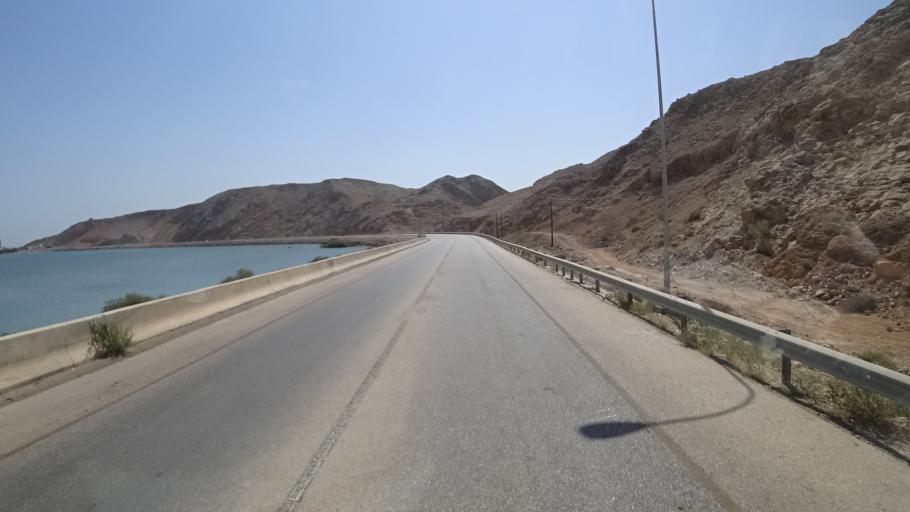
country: OM
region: Ash Sharqiyah
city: Sur
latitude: 22.5530
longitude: 59.5338
